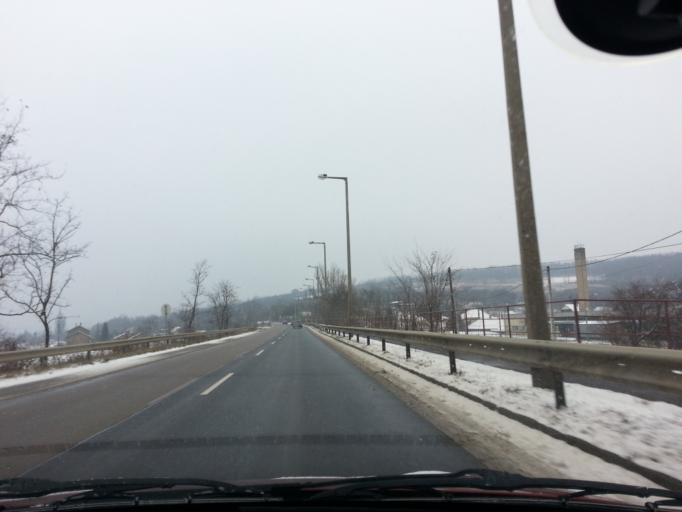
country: HU
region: Nograd
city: Salgotarjan
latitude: 48.0868
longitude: 19.7881
